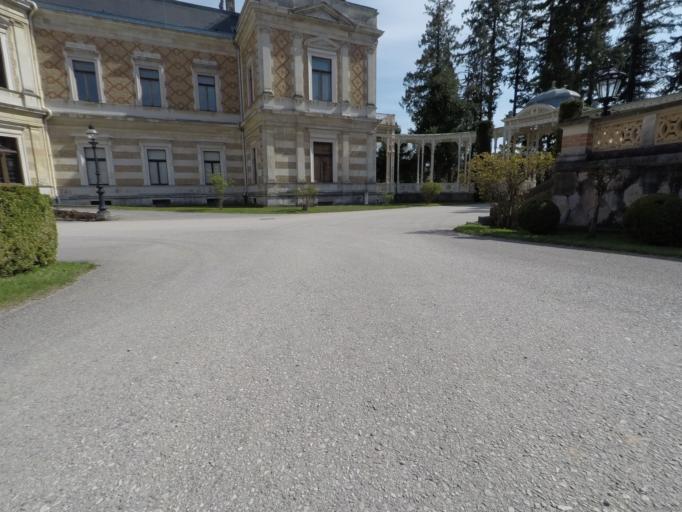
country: AT
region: Lower Austria
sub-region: Politischer Bezirk Modling
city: Perchtoldsdorf
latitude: 48.1709
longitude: 16.2457
